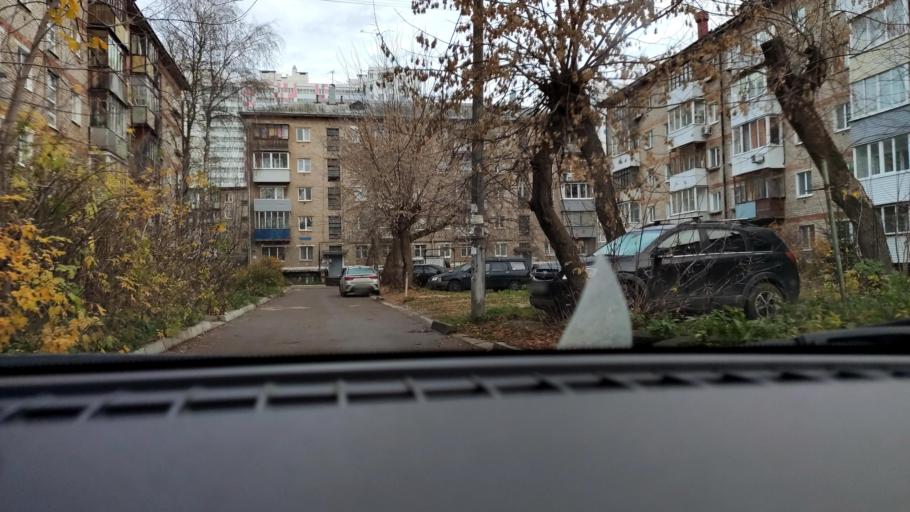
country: RU
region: Perm
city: Perm
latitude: 57.9880
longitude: 56.2636
